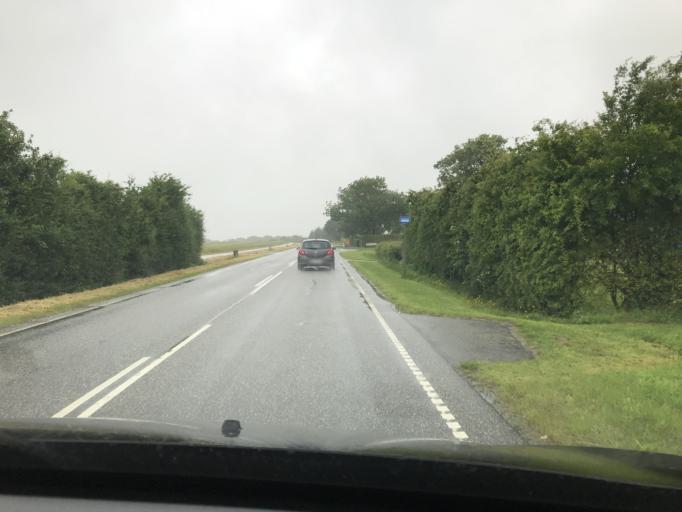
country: DK
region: South Denmark
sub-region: Haderslev Kommune
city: Starup
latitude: 55.2547
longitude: 9.6091
